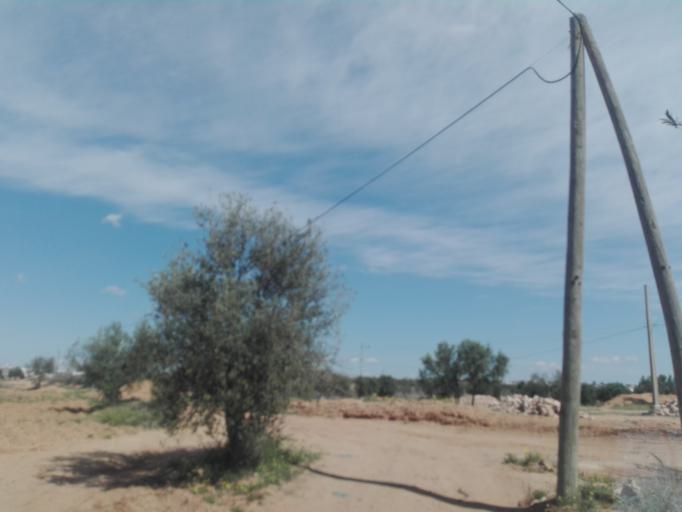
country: TN
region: Safaqis
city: Sfax
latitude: 34.7302
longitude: 10.5095
